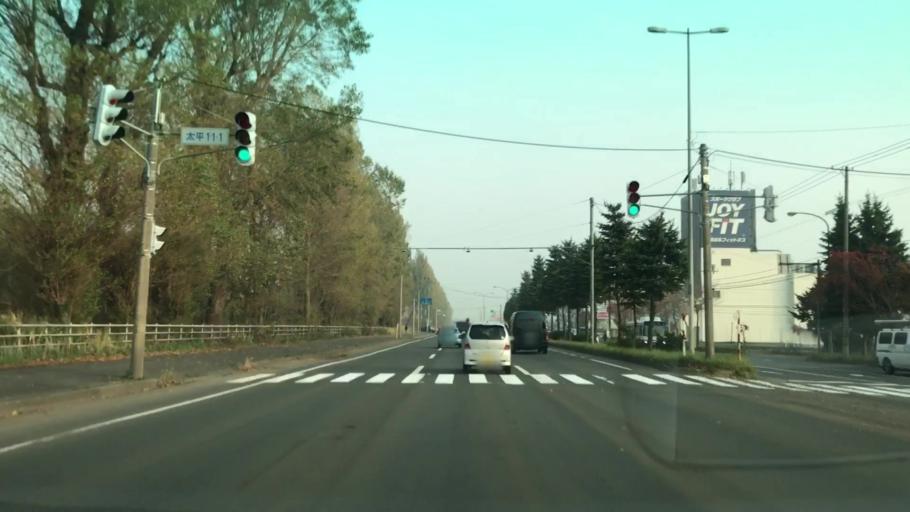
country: JP
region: Hokkaido
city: Sapporo
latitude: 43.1381
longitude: 141.3480
